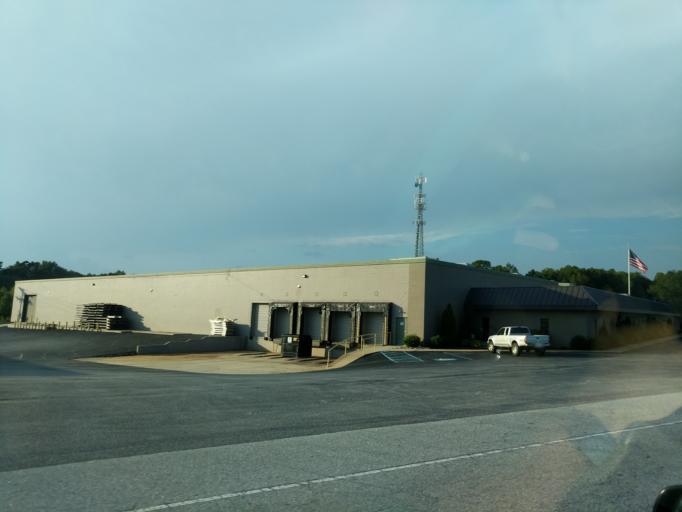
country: US
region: South Carolina
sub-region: Anderson County
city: Piedmont
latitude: 34.7028
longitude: -82.5023
